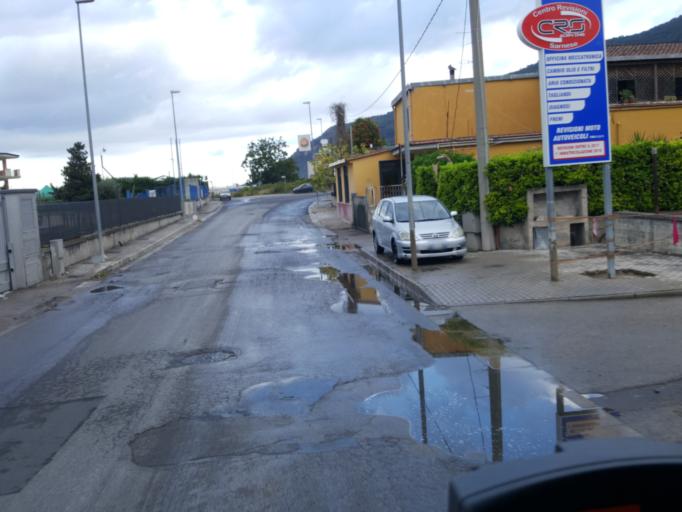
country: IT
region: Campania
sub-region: Provincia di Napoli
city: Striano
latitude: 40.8224
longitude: 14.5988
